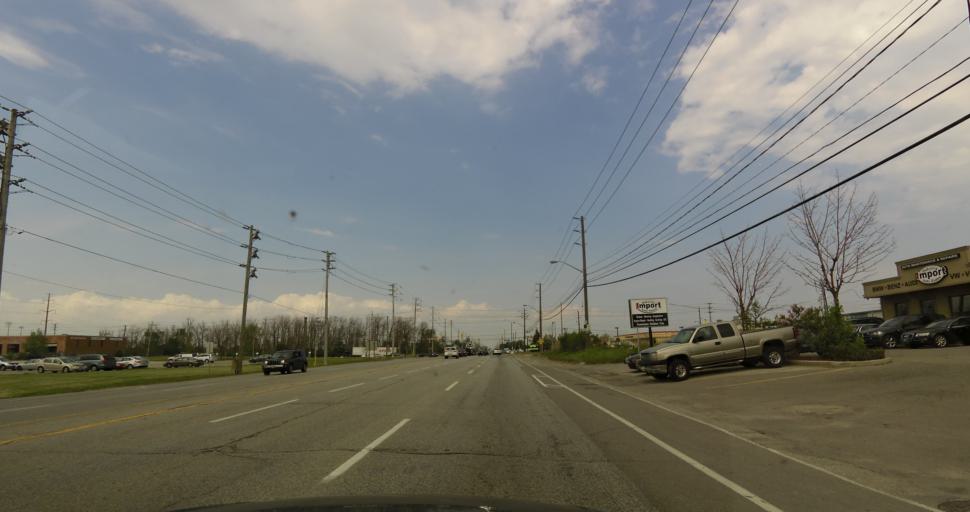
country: CA
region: Ontario
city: Oakville
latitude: 43.4953
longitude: -79.6470
